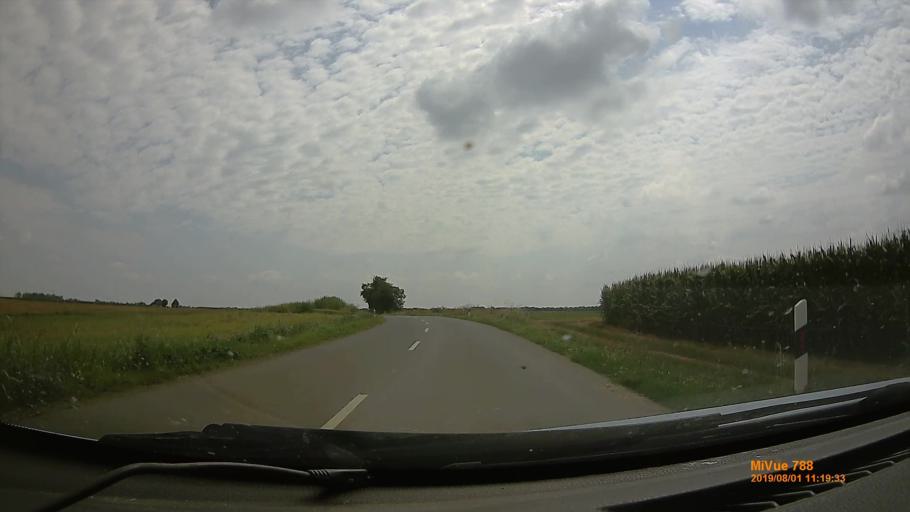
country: HU
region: Baranya
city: Kozarmisleny
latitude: 46.0083
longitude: 18.2298
